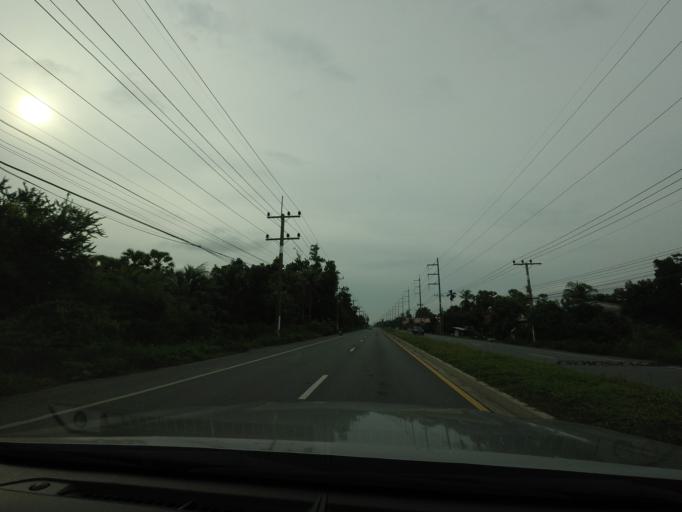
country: TH
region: Songkhla
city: Krasae Sin
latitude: 7.6959
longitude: 100.3763
